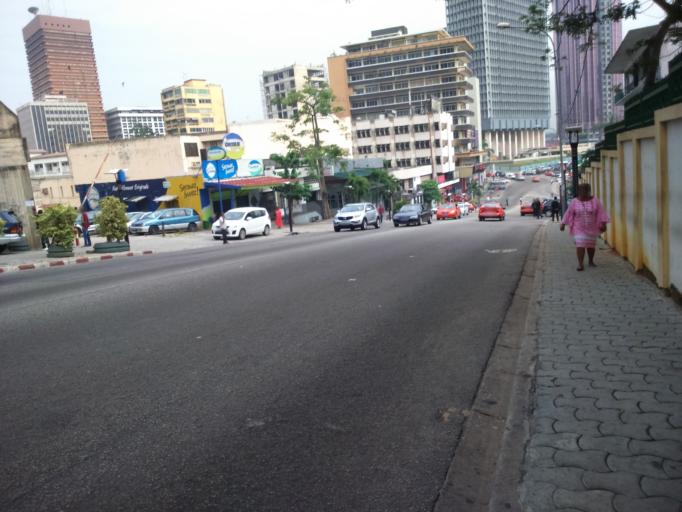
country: CI
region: Lagunes
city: Abidjan
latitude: 5.3226
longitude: -4.0162
